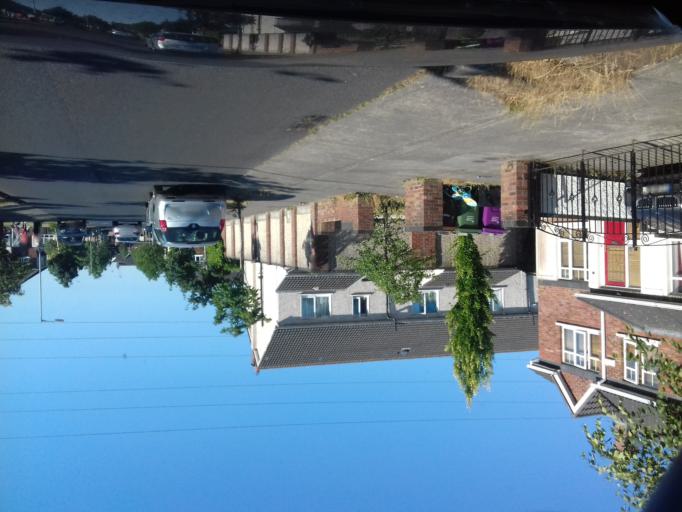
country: IE
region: Leinster
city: Hartstown
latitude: 53.3925
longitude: -6.4289
